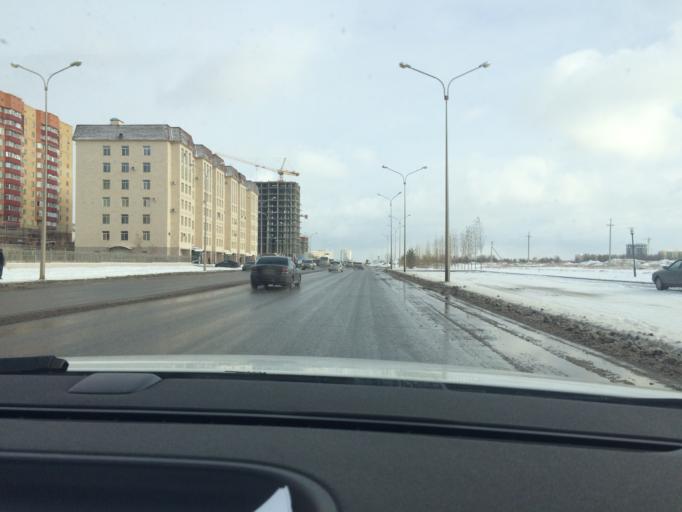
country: KZ
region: Astana Qalasy
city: Astana
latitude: 51.1226
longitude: 71.4827
